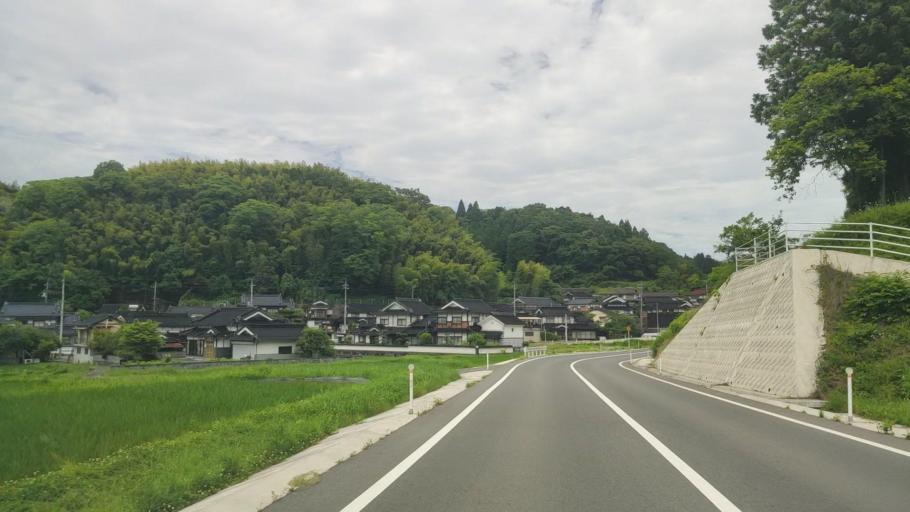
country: JP
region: Okayama
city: Tsuyama
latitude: 35.0677
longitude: 134.2355
